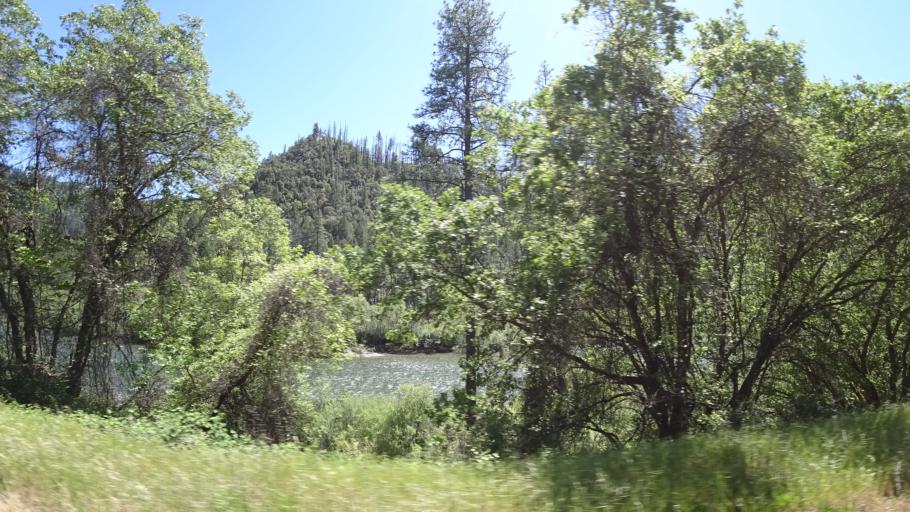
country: US
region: California
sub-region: Trinity County
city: Hayfork
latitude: 40.7843
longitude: -123.3430
